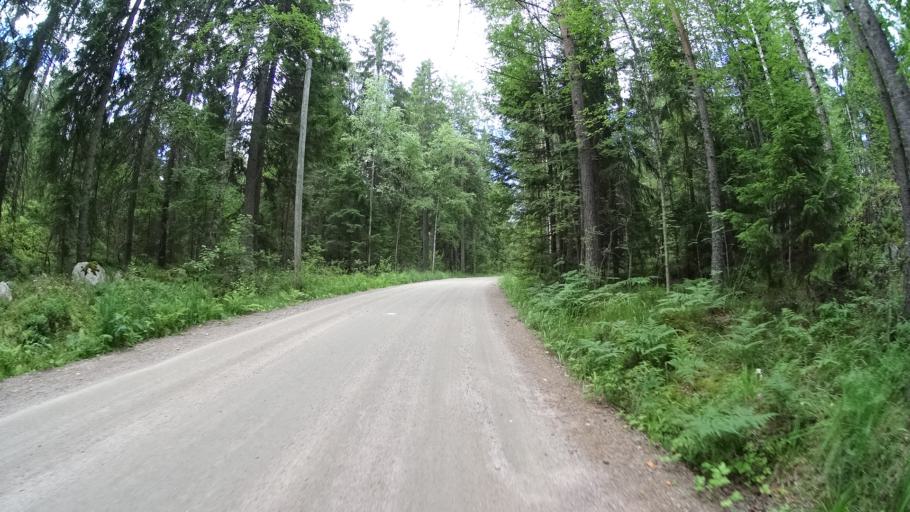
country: FI
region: Uusimaa
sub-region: Helsinki
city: Espoo
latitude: 60.2938
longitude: 24.6179
